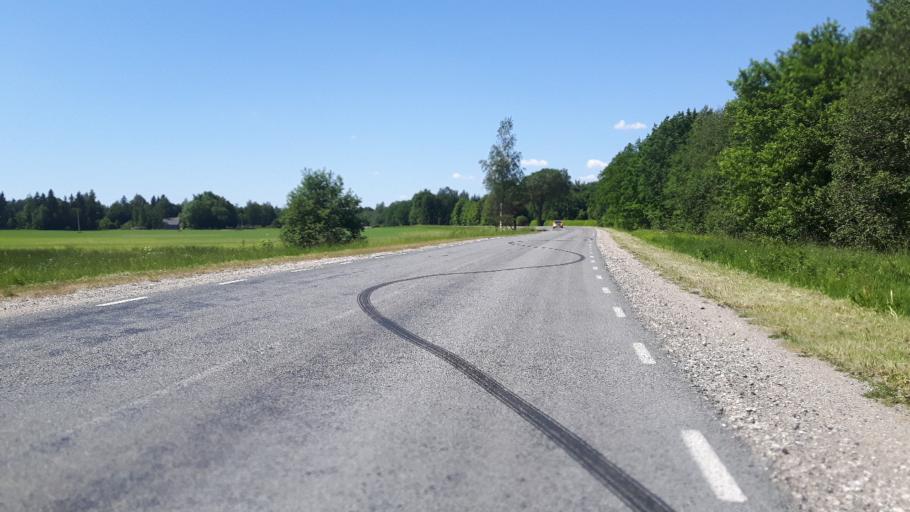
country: EE
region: Paernumaa
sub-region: Tootsi vald
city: Tootsi
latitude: 58.4976
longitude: 24.8748
